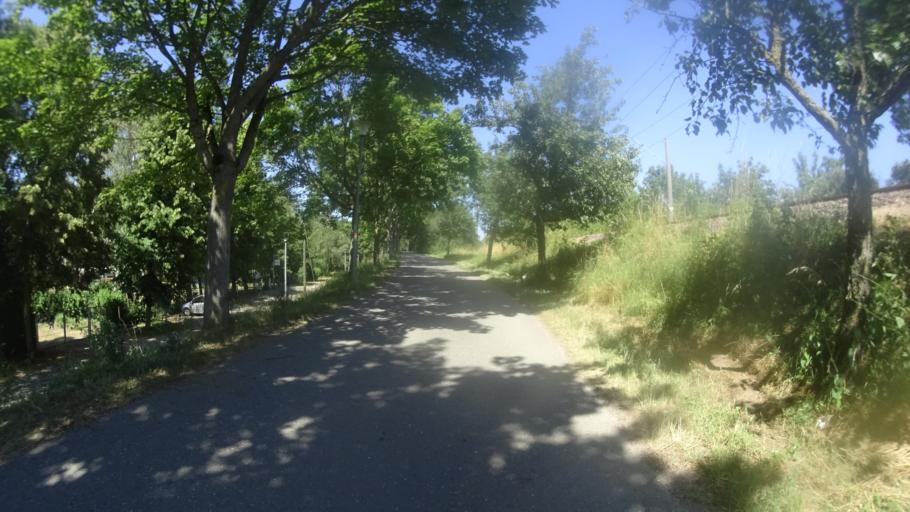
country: DE
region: Baden-Wuerttemberg
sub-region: Karlsruhe Region
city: Karlsruhe
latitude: 49.0058
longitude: 8.4702
